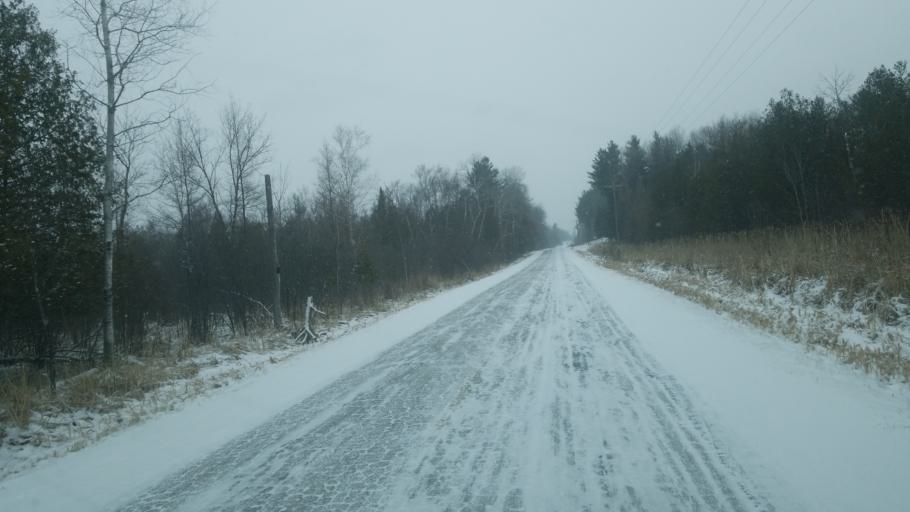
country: US
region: Michigan
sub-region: Mecosta County
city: Big Rapids
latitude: 43.7946
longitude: -85.4026
